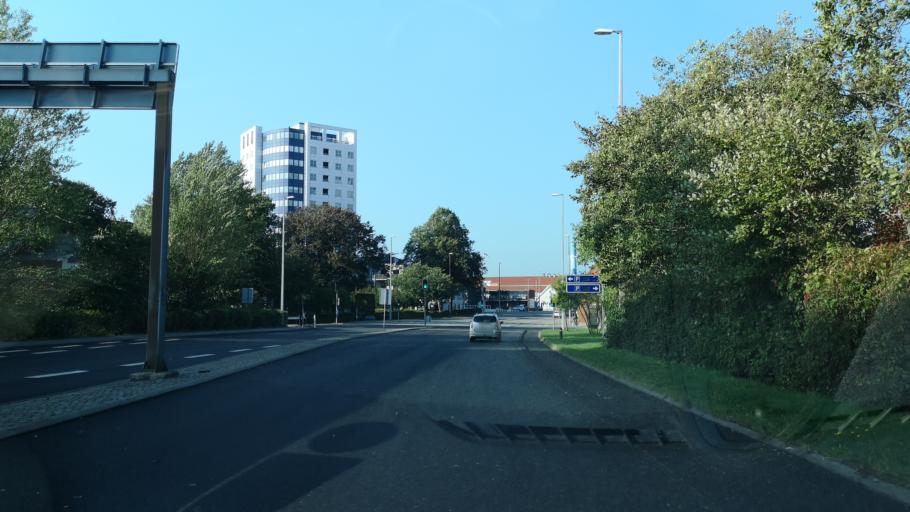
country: DK
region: Central Jutland
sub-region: Herning Kommune
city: Herning
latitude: 56.1342
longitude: 8.9673
